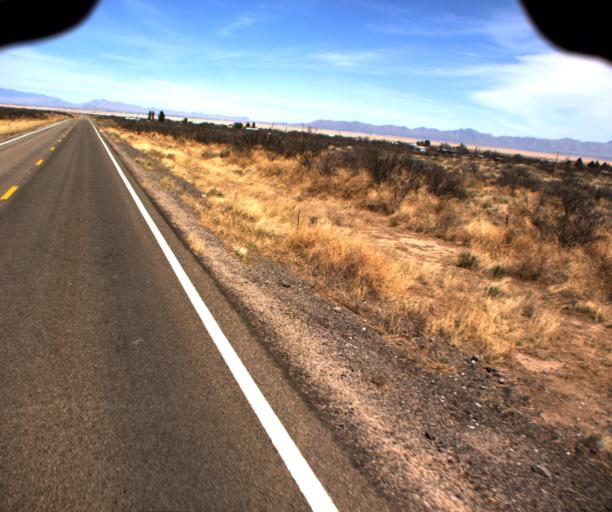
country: US
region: Arizona
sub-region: Cochise County
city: Willcox
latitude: 32.1155
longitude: -109.9119
